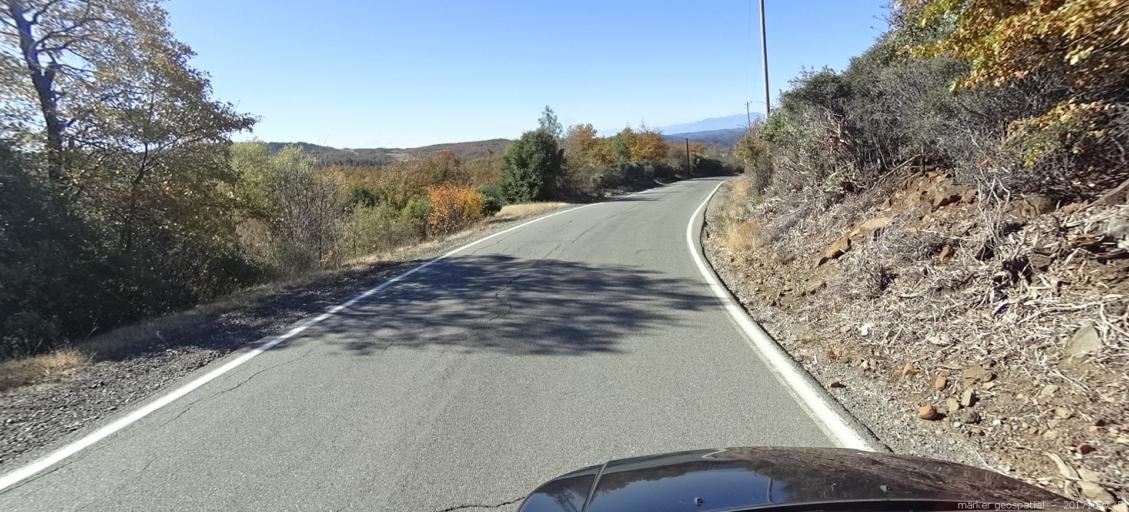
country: US
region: California
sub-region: Shasta County
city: Burney
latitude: 40.7971
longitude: -121.9148
